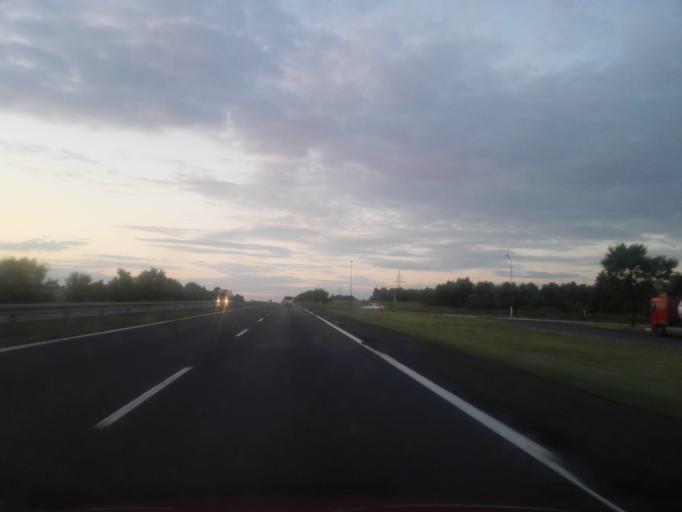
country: PL
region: Lodz Voivodeship
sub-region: Powiat radomszczanski
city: Gomunice
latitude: 51.1798
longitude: 19.4687
